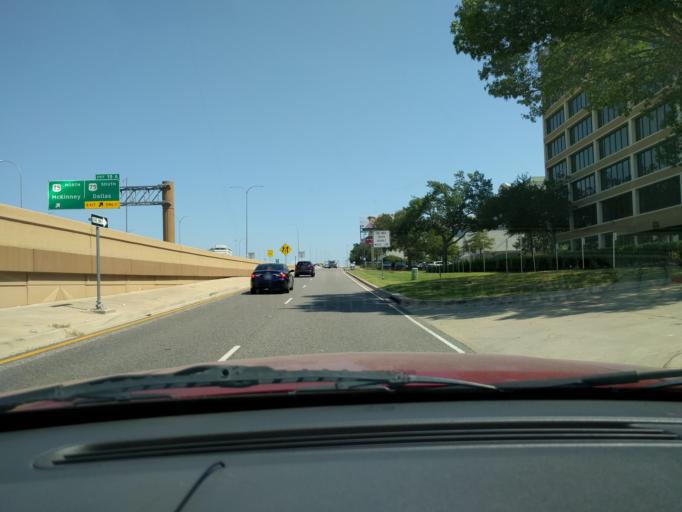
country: US
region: Texas
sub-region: Dallas County
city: Richardson
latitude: 32.9236
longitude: -96.7763
